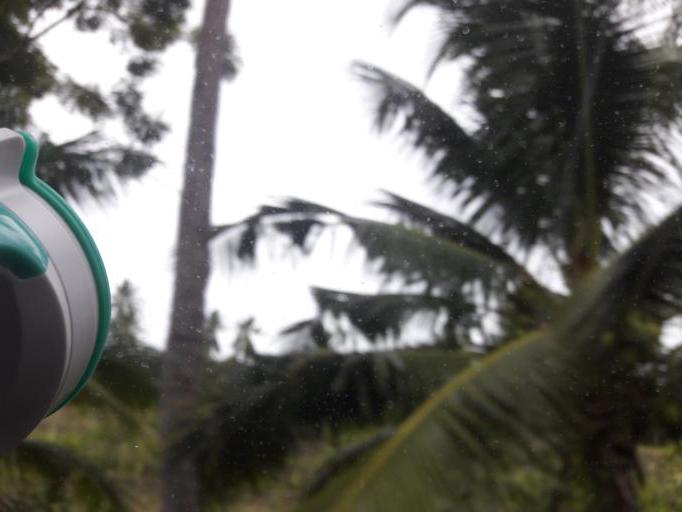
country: TH
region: Ratchaburi
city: Damnoen Saduak
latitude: 13.5378
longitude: 100.0050
